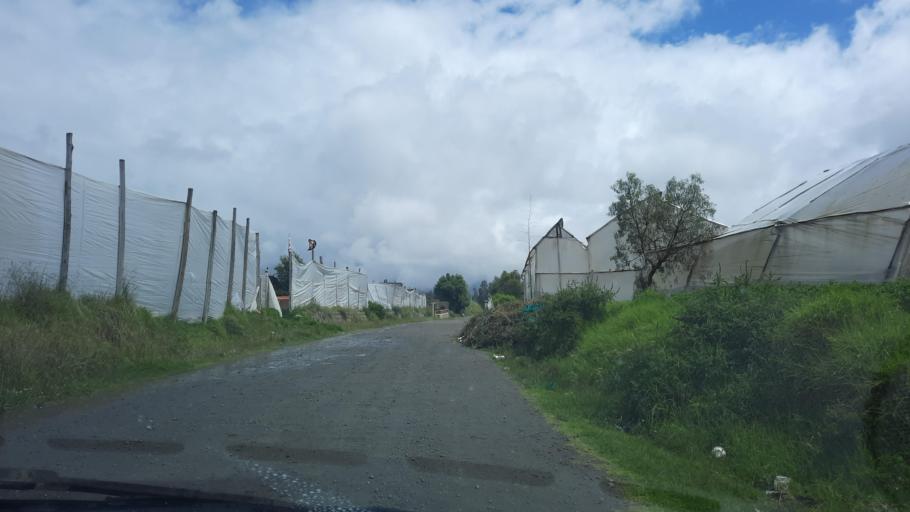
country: EC
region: Chimborazo
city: Riobamba
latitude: -1.6903
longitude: -78.6679
